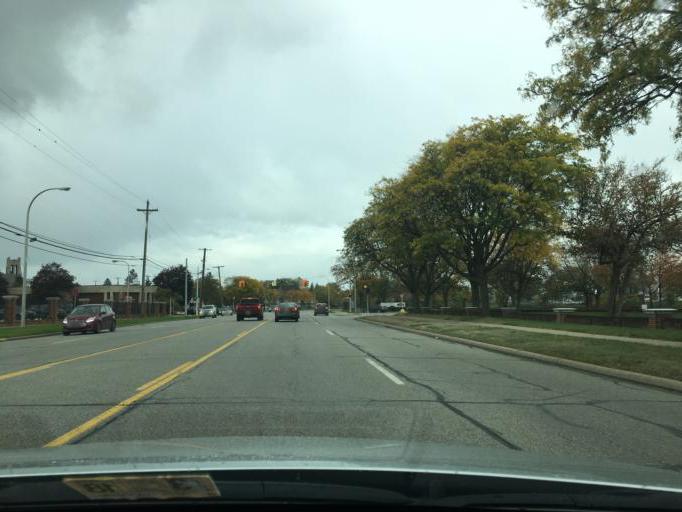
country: US
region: Michigan
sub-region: Wayne County
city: Dearborn Heights
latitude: 42.3021
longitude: -83.2381
